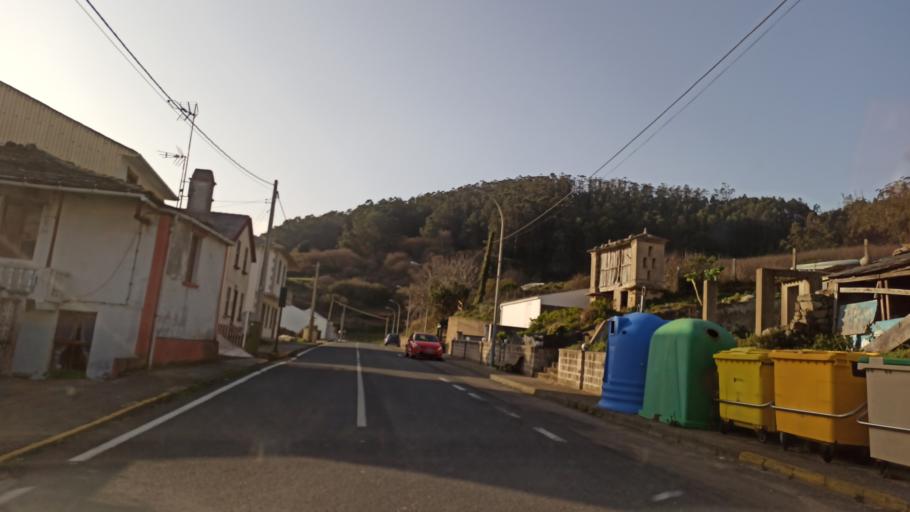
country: ES
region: Galicia
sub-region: Provincia de Lugo
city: Viveiro
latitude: 43.7732
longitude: -7.6694
